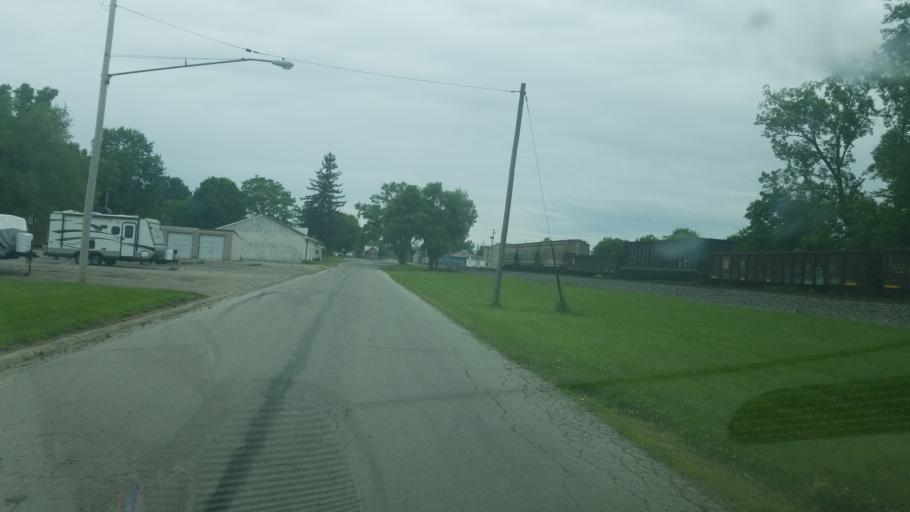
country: US
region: Ohio
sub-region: Crawford County
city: Bucyrus
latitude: 40.8030
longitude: -82.9673
